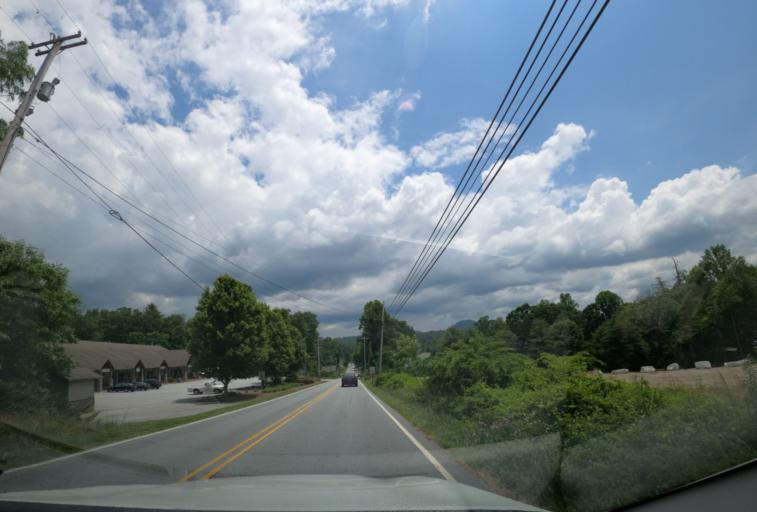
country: US
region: North Carolina
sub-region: Jackson County
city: Cullowhee
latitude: 35.1132
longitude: -83.1094
